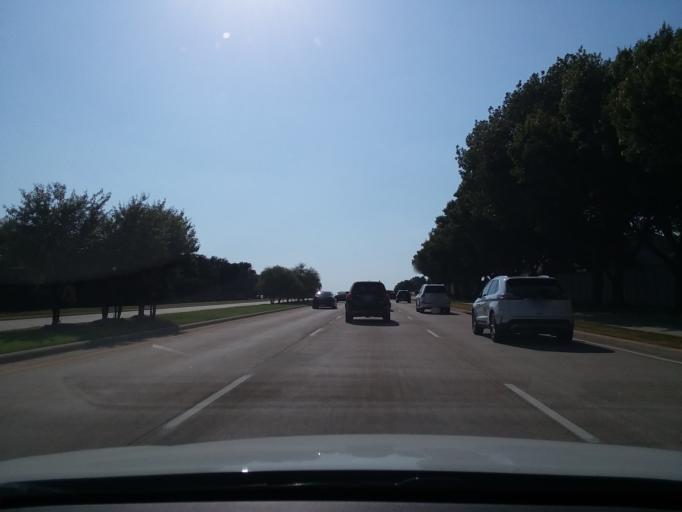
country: US
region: Texas
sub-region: Denton County
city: Flower Mound
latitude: 33.0139
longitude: -97.0650
